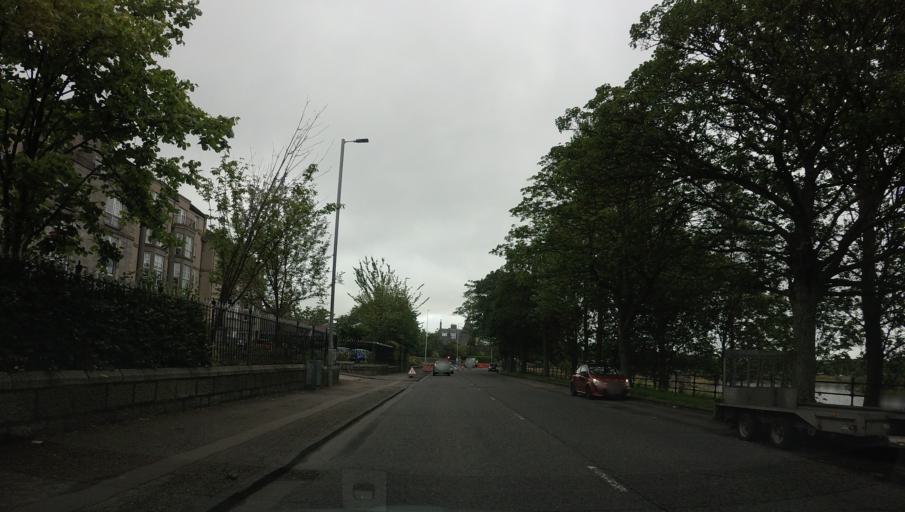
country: GB
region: Scotland
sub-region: Aberdeen City
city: Aberdeen
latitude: 57.1273
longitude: -2.1170
